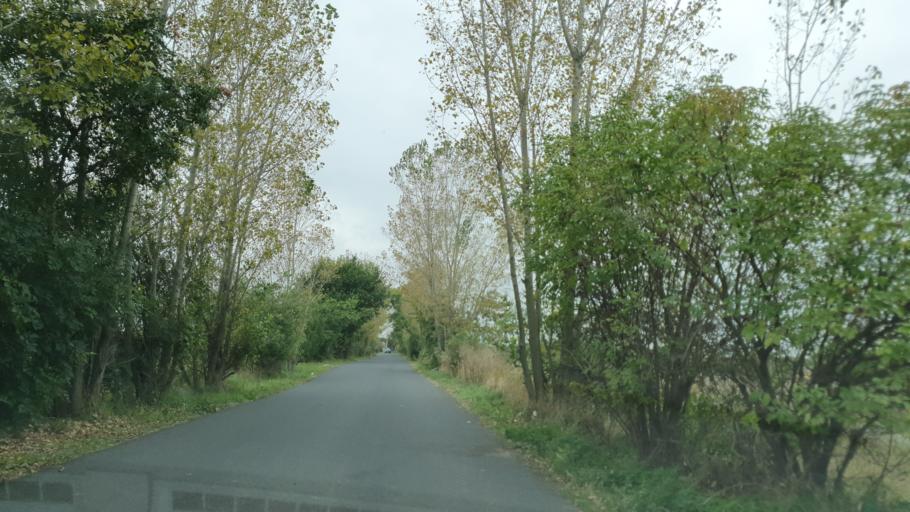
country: HU
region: Pest
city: Dunaharaszti
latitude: 47.3819
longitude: 19.0861
